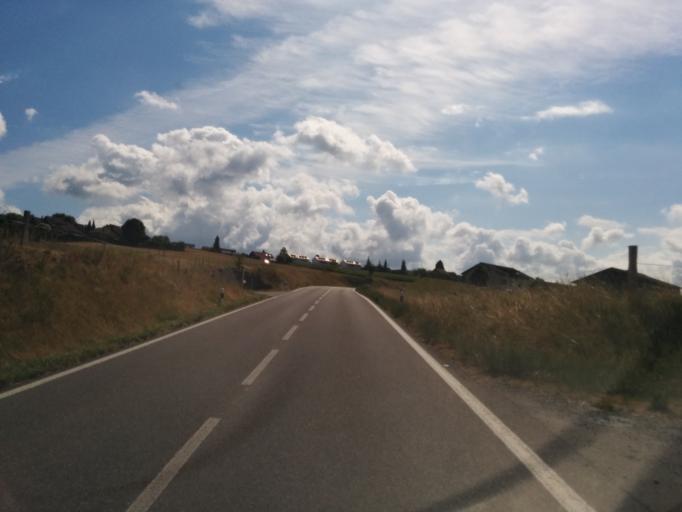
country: CH
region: Aargau
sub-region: Bezirk Bremgarten
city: Berikon
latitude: 47.3465
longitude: 8.3726
